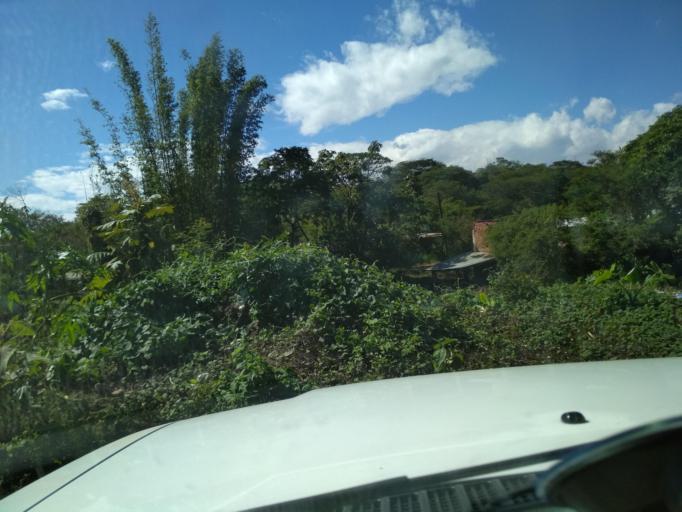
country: MX
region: Veracruz
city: El Castillo
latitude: 19.5485
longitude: -96.8534
